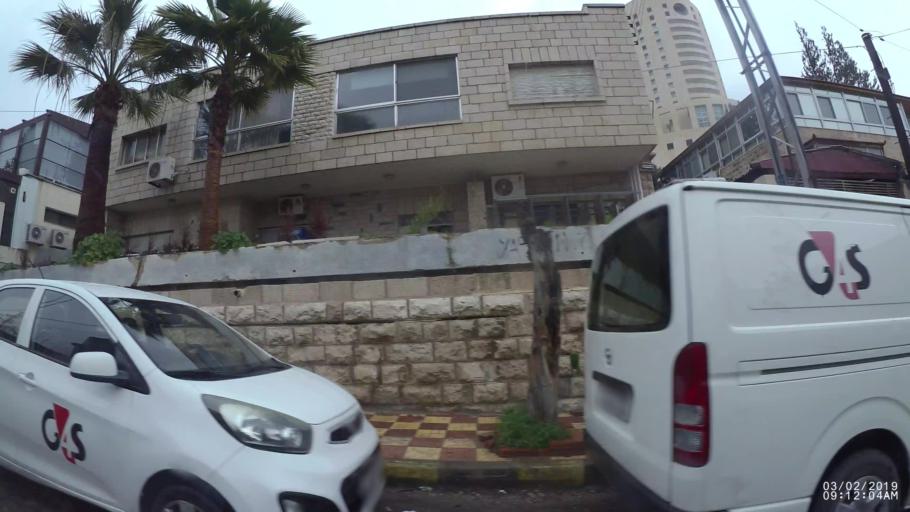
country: JO
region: Amman
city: Amman
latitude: 31.9523
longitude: 35.9076
